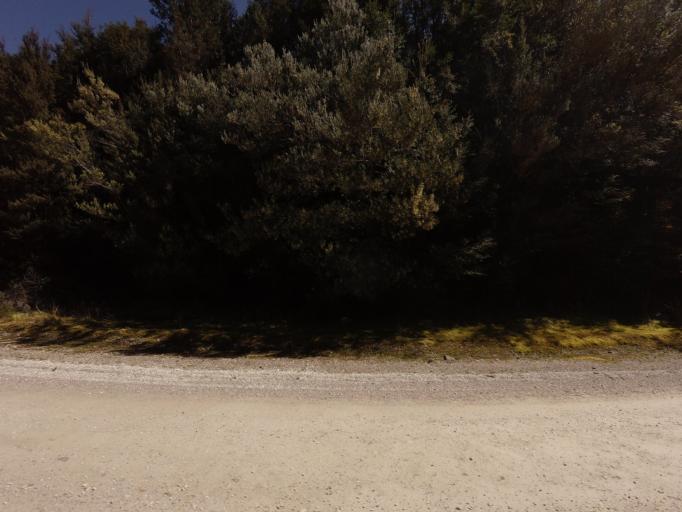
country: AU
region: Tasmania
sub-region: Huon Valley
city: Geeveston
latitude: -42.8351
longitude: 146.3800
